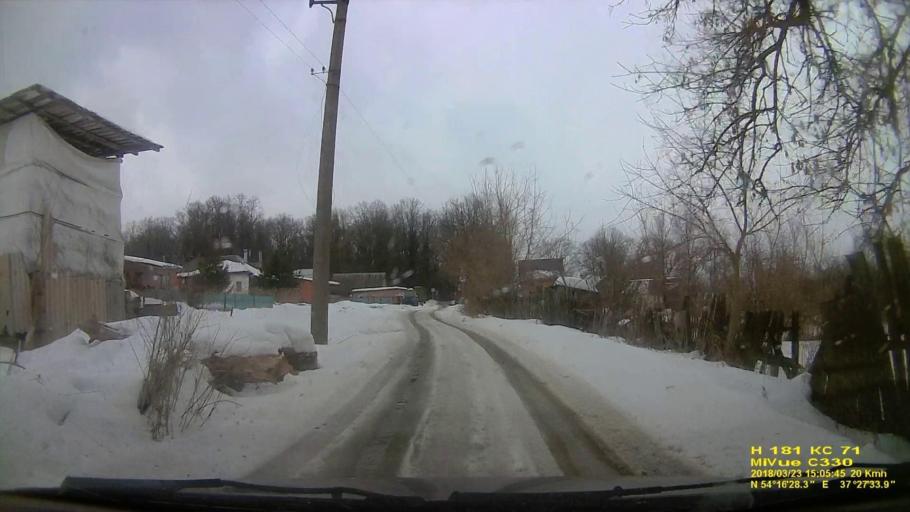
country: RU
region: Tula
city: Leninskiy
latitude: 54.2746
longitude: 37.4593
